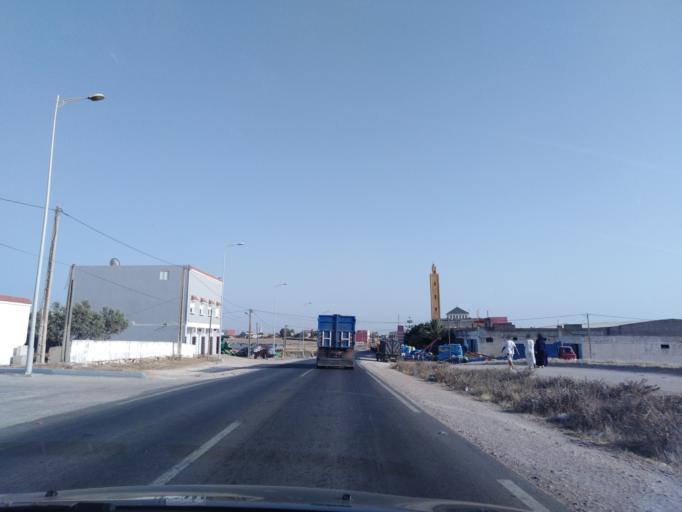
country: MA
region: Doukkala-Abda
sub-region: El-Jadida
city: Sidi Bennour
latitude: 32.5564
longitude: -8.7249
